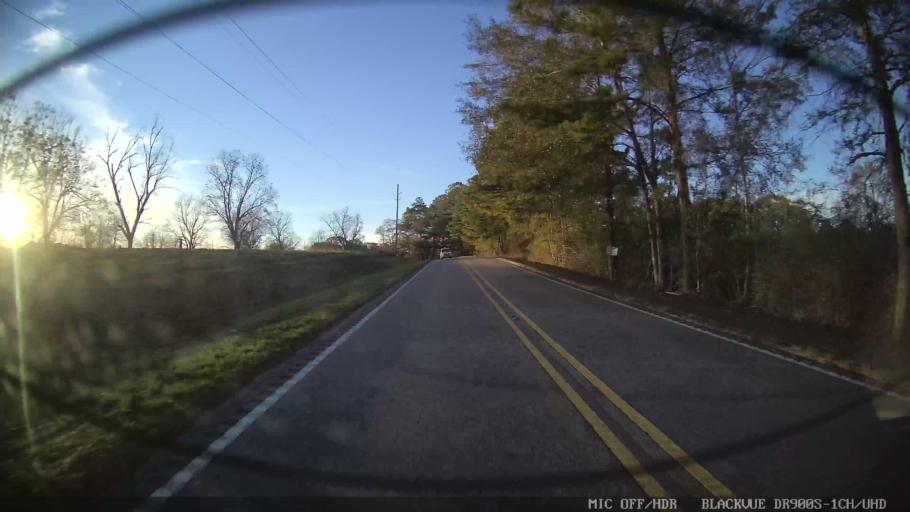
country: US
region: Mississippi
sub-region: Lamar County
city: Lumberton
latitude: 30.9950
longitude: -89.3841
